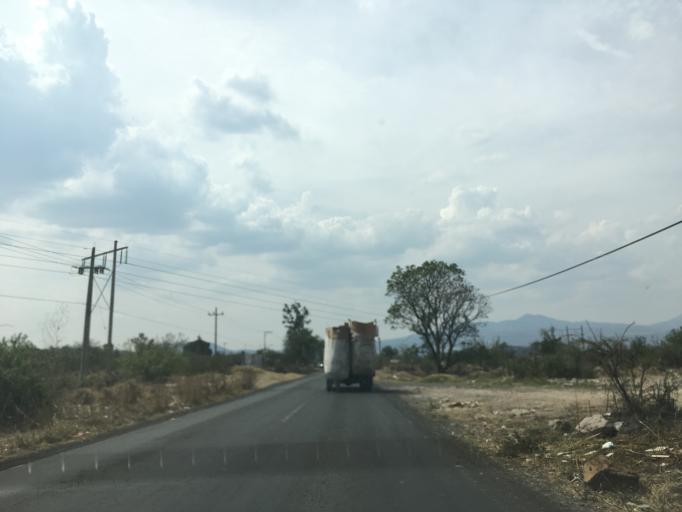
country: MX
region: Michoacan
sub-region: Morelia
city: La Mintzita (Piedra Dura)
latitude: 19.6415
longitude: -101.2778
